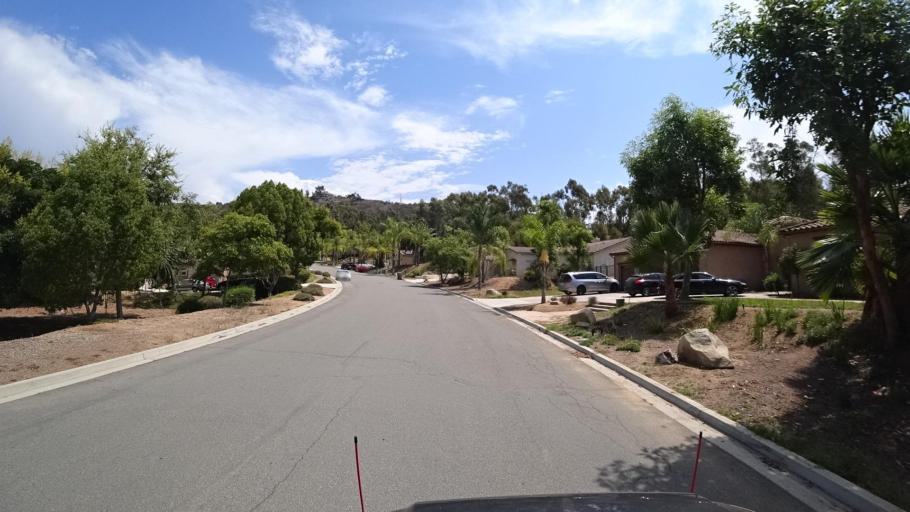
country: US
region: California
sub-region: San Diego County
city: Hidden Meadows
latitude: 33.1830
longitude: -117.0912
